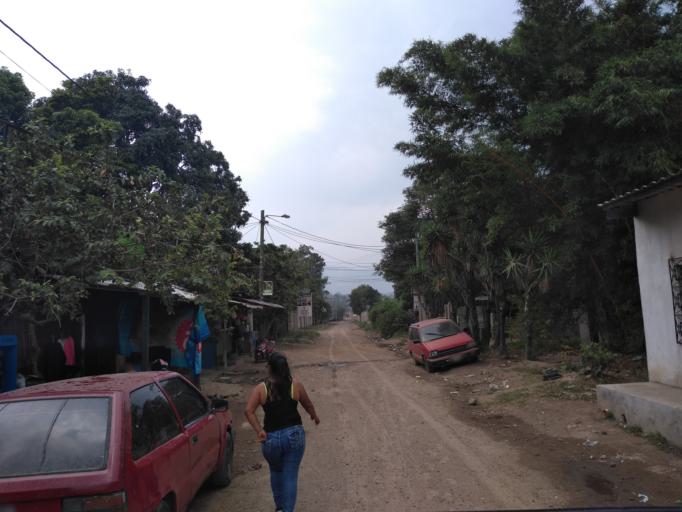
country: GT
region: Guatemala
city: Petapa
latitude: 14.5124
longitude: -90.5557
